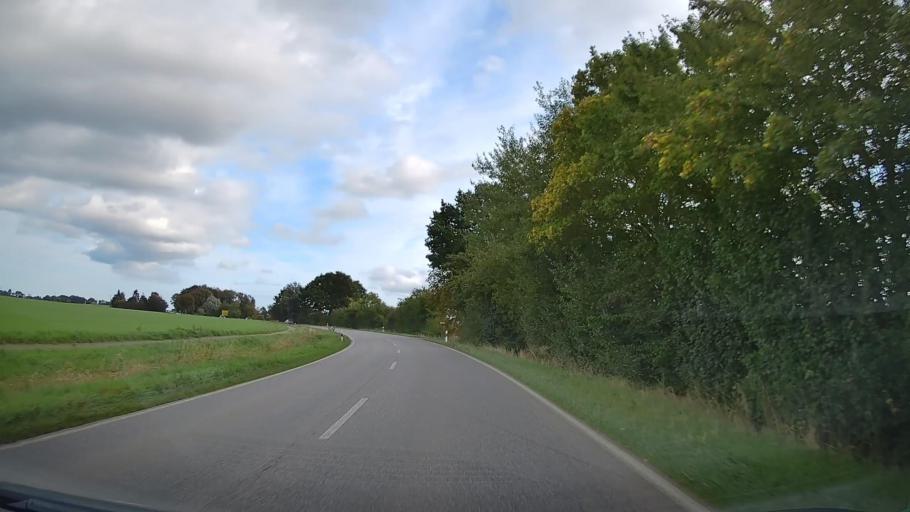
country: DE
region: Schleswig-Holstein
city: Niesgrau
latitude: 54.7514
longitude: 9.8134
